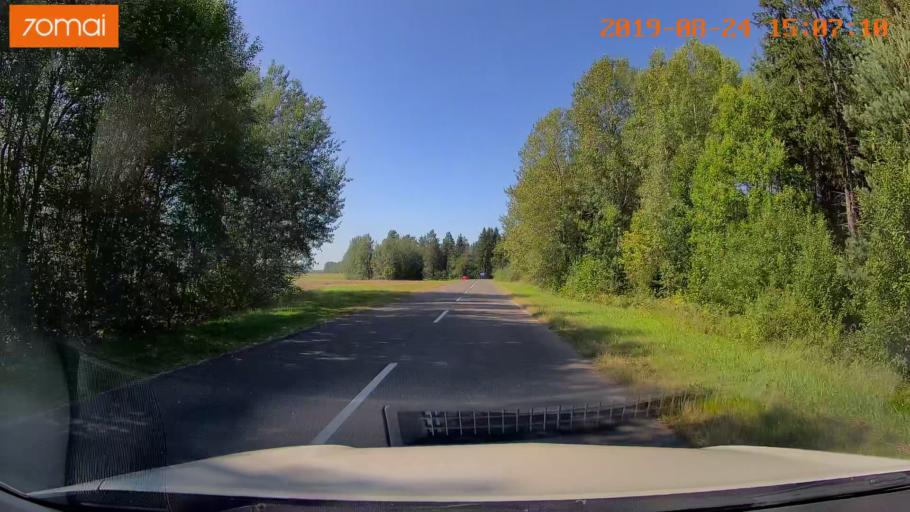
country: BY
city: Michanovichi
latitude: 53.6070
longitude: 27.6761
